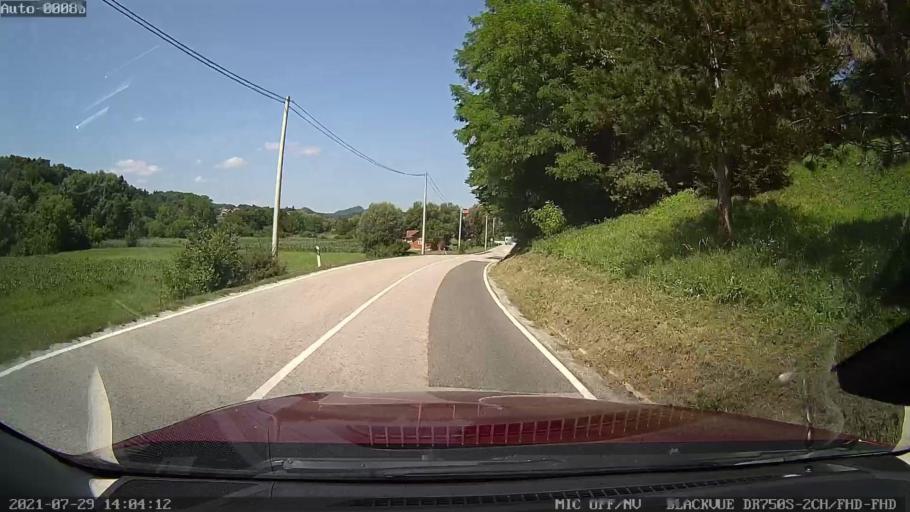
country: HR
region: Varazdinska
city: Lepoglava
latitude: 46.2403
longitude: 15.9624
